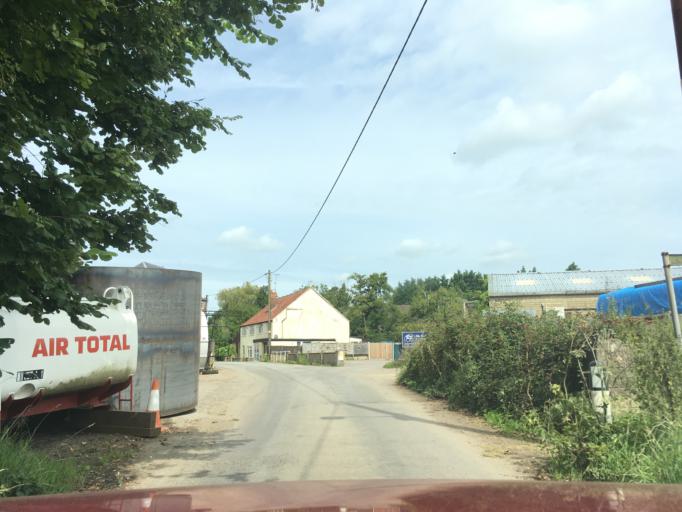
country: GB
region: England
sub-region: South Gloucestershire
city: Charfield
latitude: 51.6344
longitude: -2.4022
